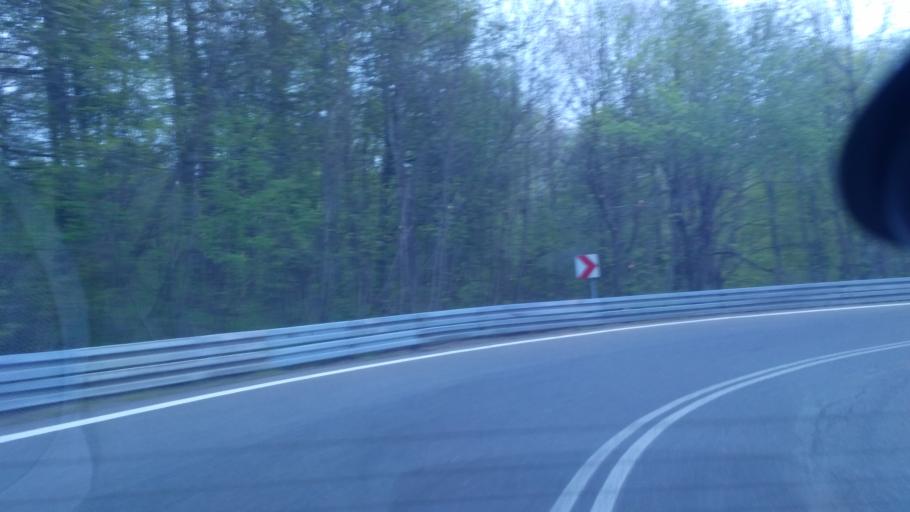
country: PL
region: Subcarpathian Voivodeship
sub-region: Powiat sanocki
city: Tyrawa Woloska
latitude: 49.5575
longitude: 22.3274
